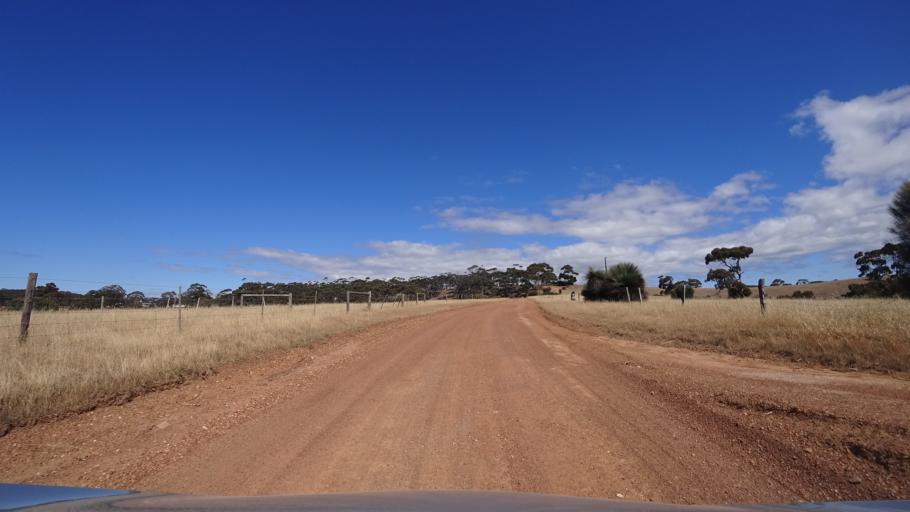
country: AU
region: South Australia
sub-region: Kangaroo Island
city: Kingscote
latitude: -35.6885
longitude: 136.9798
